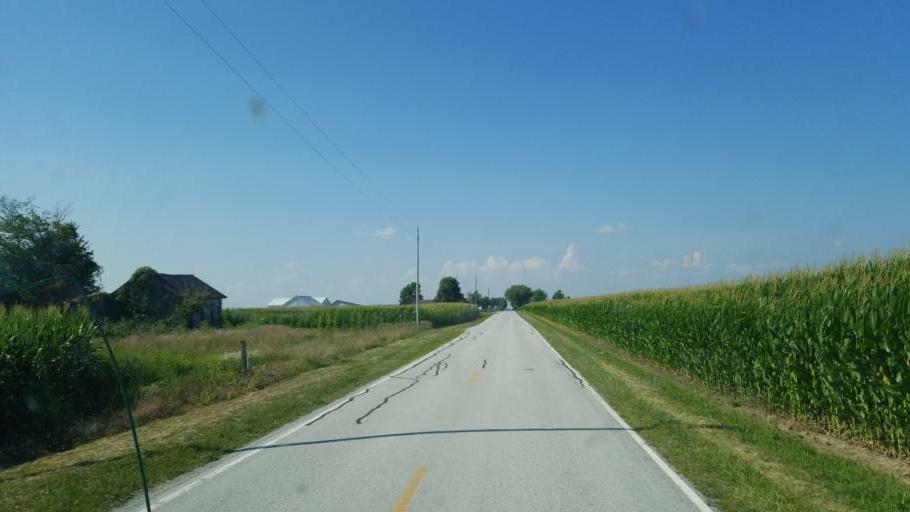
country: US
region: Ohio
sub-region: Hardin County
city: Forest
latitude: 40.7100
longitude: -83.4958
